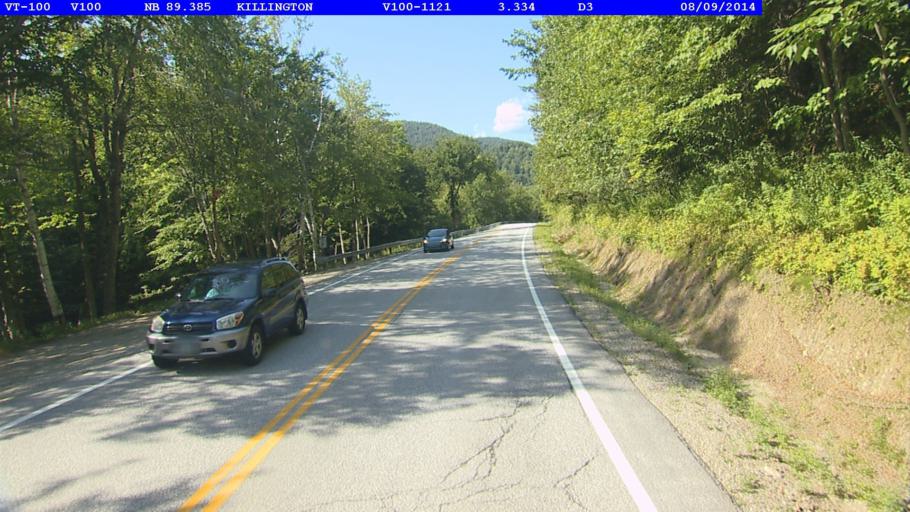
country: US
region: Vermont
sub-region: Rutland County
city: Rutland
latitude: 43.7093
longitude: -72.8259
